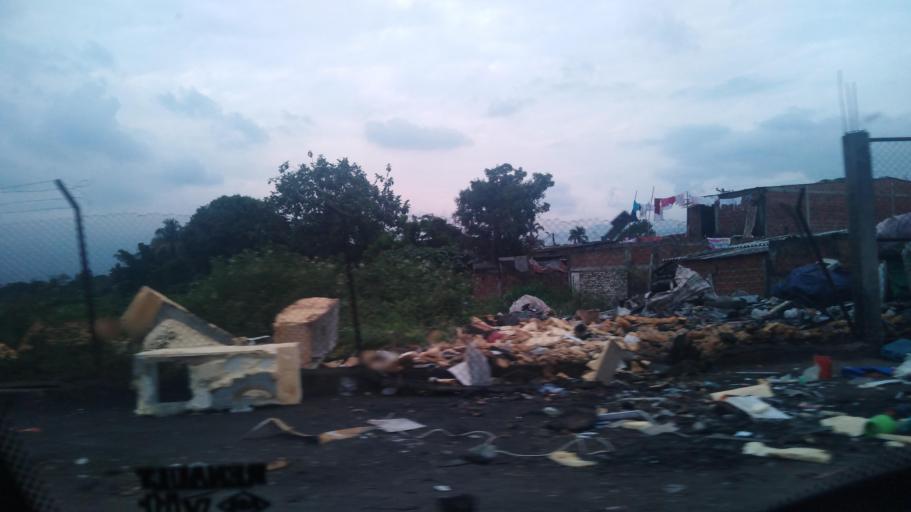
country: CO
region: Valle del Cauca
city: Cali
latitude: 3.4358
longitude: -76.4842
